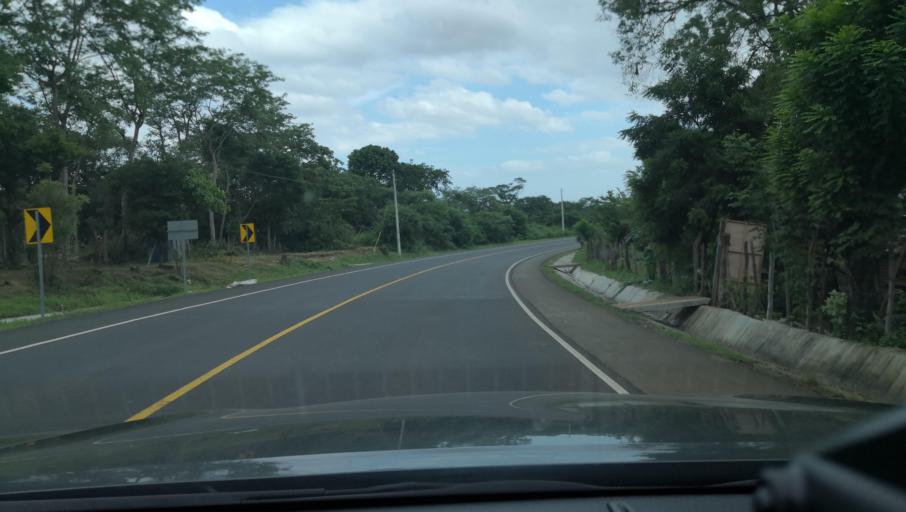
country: NI
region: Masaya
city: Nindiri
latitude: 12.0582
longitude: -86.1382
